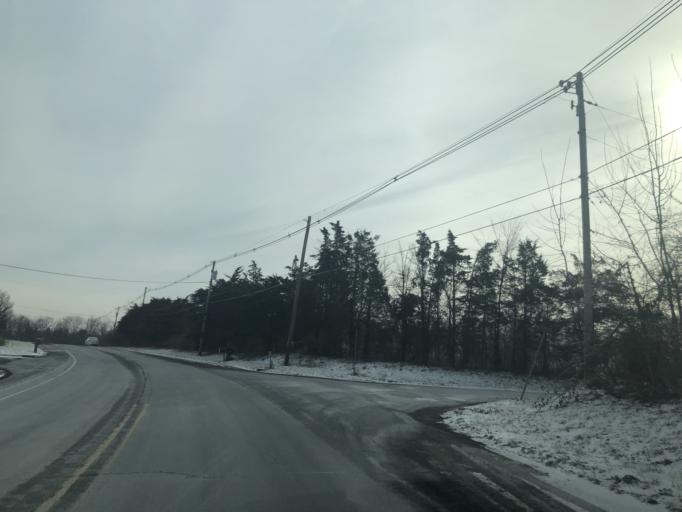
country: US
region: New Jersey
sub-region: Warren County
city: Belvidere
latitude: 40.9339
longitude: -75.0139
